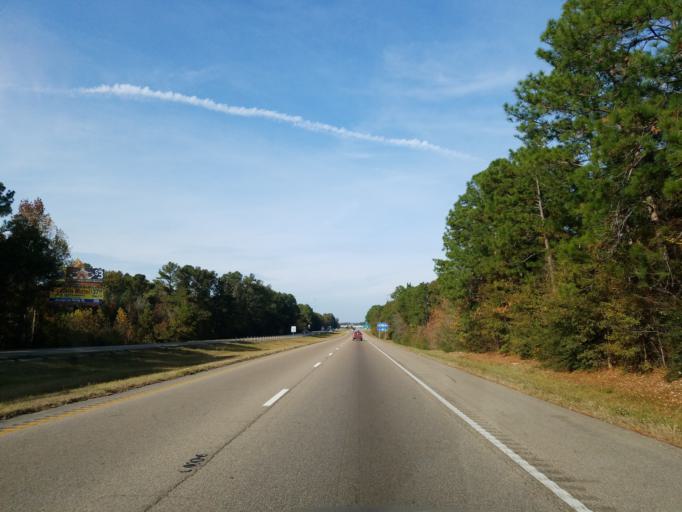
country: US
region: Mississippi
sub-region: Lamar County
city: West Hattiesburg
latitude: 31.3129
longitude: -89.3523
